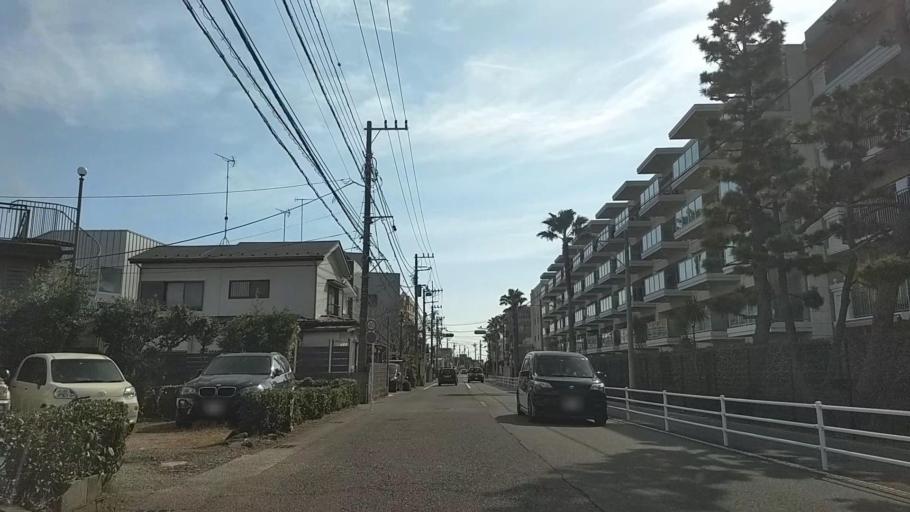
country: JP
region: Kanagawa
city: Fujisawa
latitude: 35.3223
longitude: 139.4540
